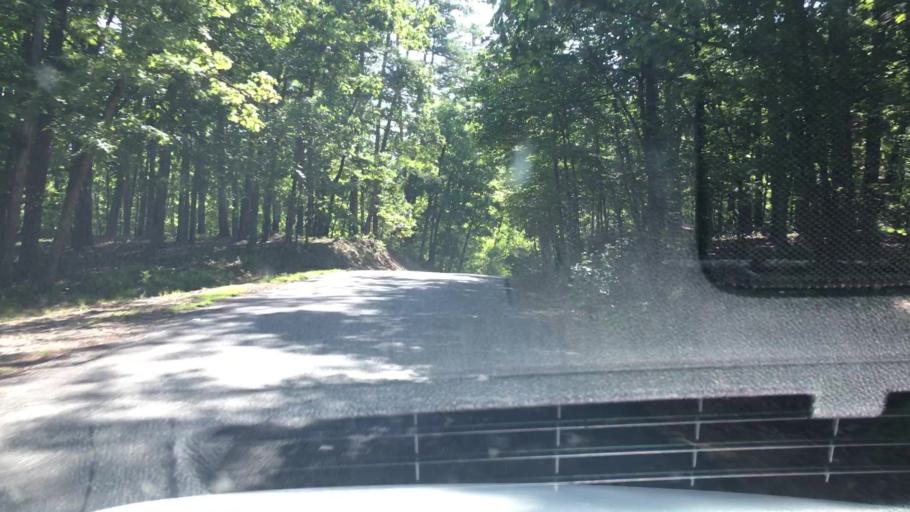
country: US
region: Arkansas
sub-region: Garland County
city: Piney
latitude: 34.5422
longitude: -93.3564
